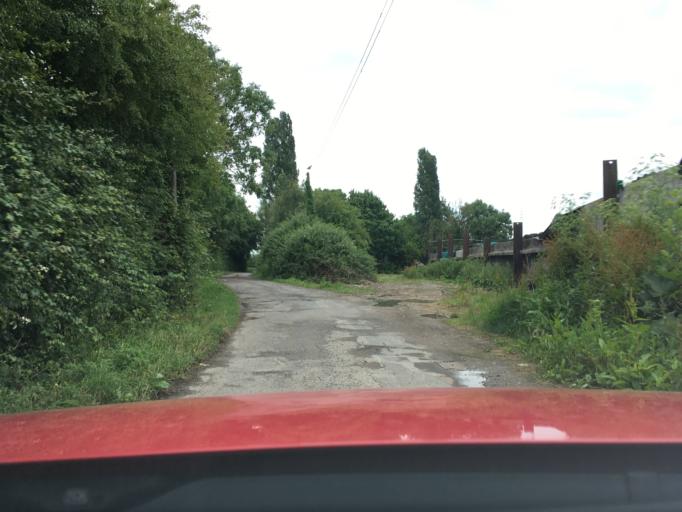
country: GB
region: England
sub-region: Gloucestershire
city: Cinderford
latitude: 51.7900
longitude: -2.4286
